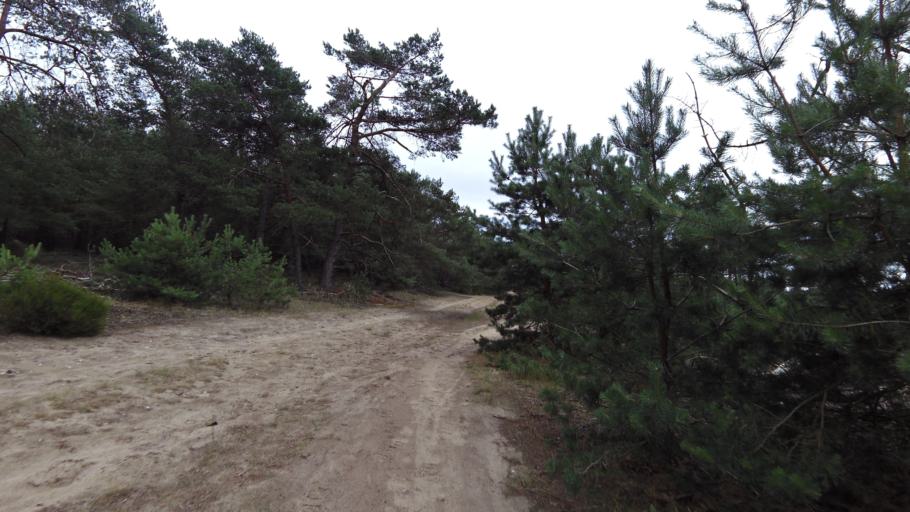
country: NL
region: Gelderland
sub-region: Gemeente Apeldoorn
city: Uddel
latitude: 52.2281
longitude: 5.8040
